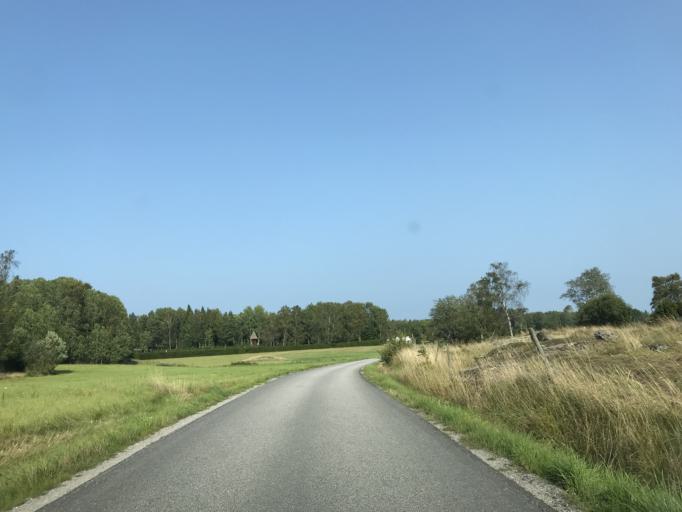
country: SE
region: Stockholm
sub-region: Norrtalje Kommun
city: Bjorko
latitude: 59.8523
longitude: 19.0140
